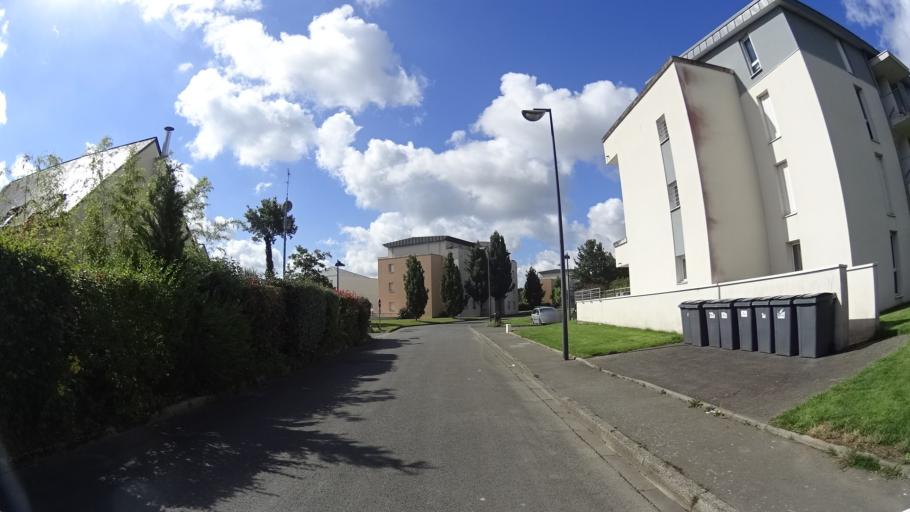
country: FR
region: Brittany
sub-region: Departement d'Ille-et-Vilaine
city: Saint-Gilles
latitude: 48.1293
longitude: -1.8095
